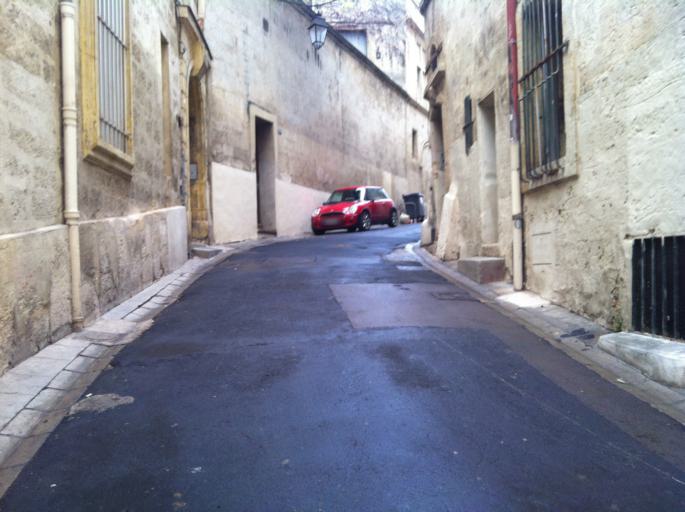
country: FR
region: Languedoc-Roussillon
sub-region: Departement de l'Herault
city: Montpellier
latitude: 43.6127
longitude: 3.8784
